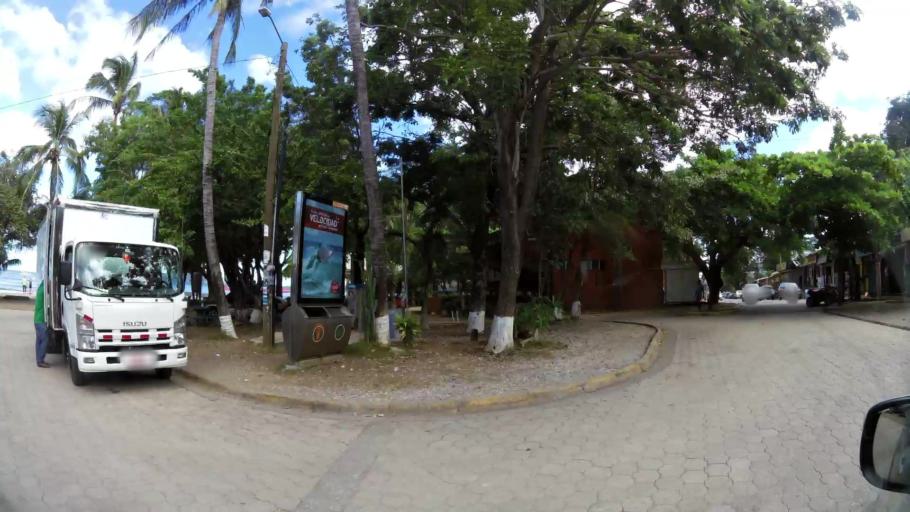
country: CR
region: Guanacaste
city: Santa Cruz
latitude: 10.2985
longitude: -85.8425
